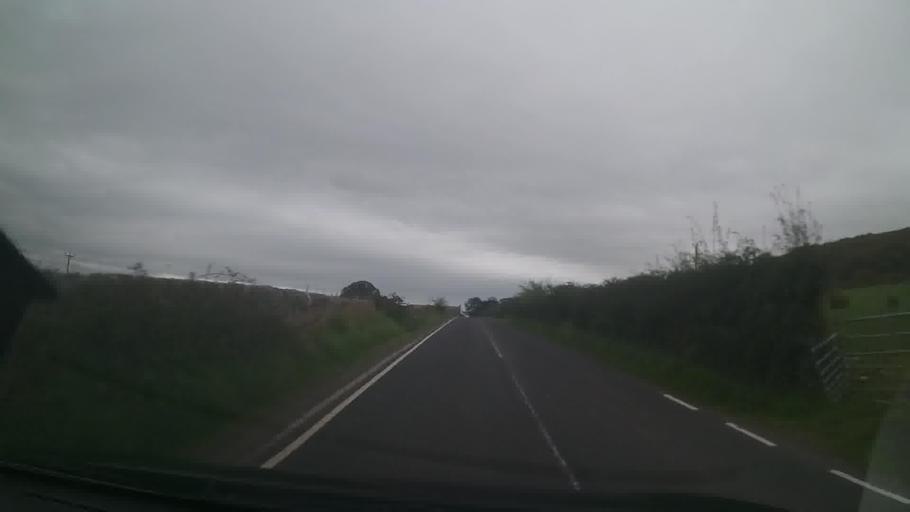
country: GB
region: Scotland
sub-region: Argyll and Bute
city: Port Bannatyne
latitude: 55.8783
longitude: -5.0845
